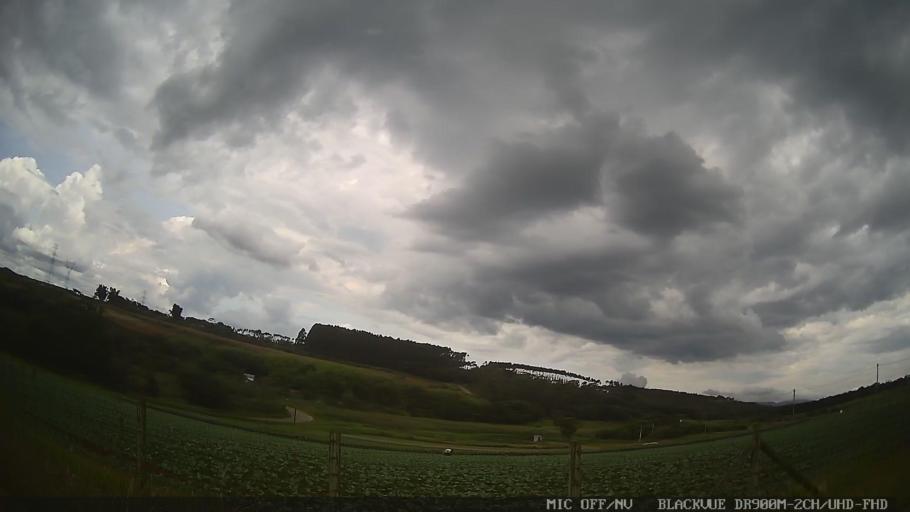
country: BR
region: Sao Paulo
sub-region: Suzano
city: Suzano
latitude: -23.6614
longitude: -46.2805
